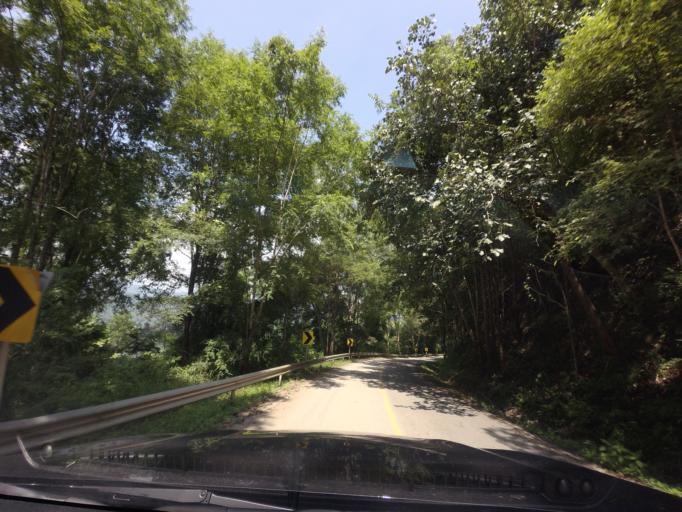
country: TH
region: Loei
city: Na Haeo
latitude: 17.6225
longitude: 100.8993
